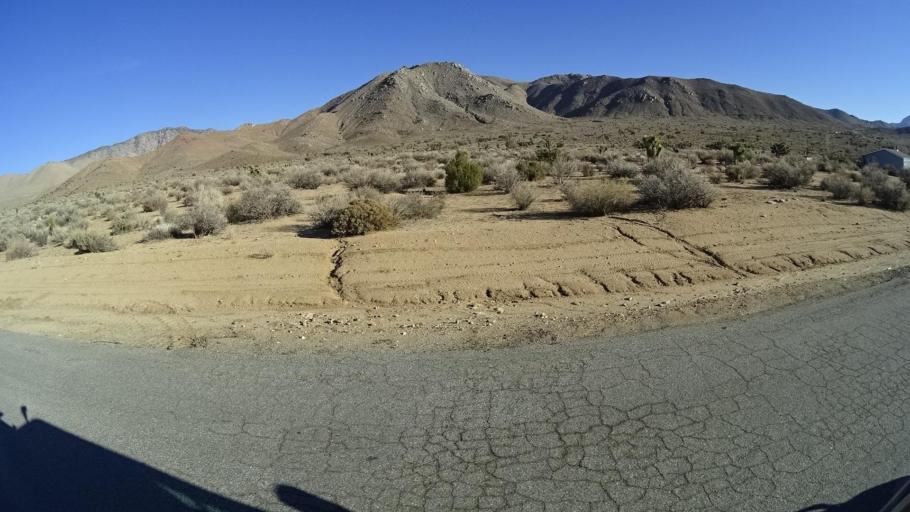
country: US
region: California
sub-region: Kern County
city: Weldon
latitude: 35.5472
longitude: -118.2062
